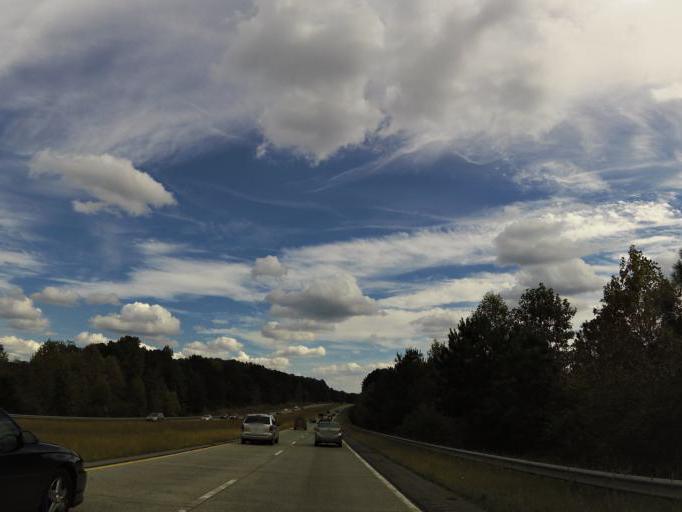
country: US
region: Georgia
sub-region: Pickens County
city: Jasper
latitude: 34.4445
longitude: -84.4435
